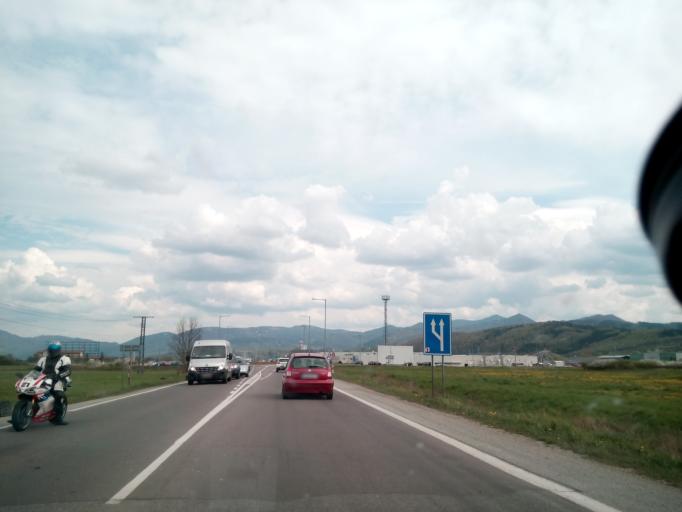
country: SK
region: Zilinsky
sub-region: Okres Martin
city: Martin
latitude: 49.0943
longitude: 18.9568
